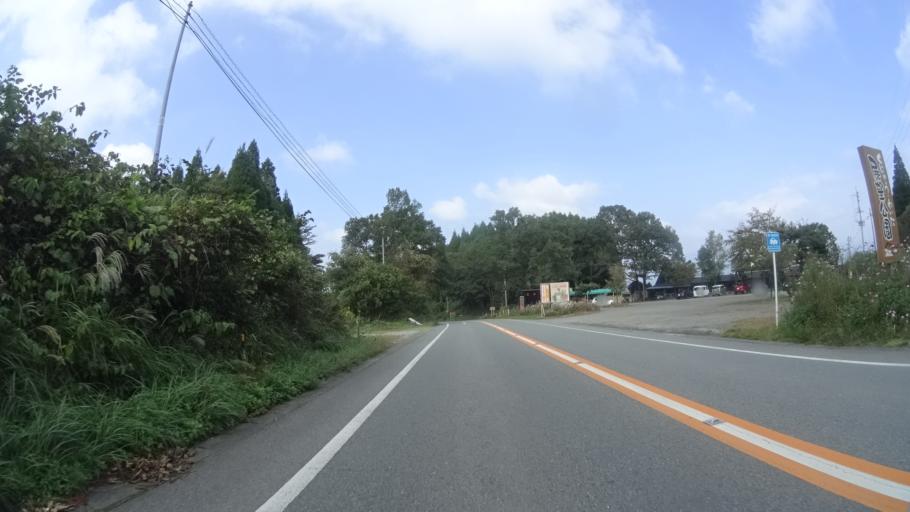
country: JP
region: Kumamoto
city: Aso
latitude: 33.0646
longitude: 131.0671
